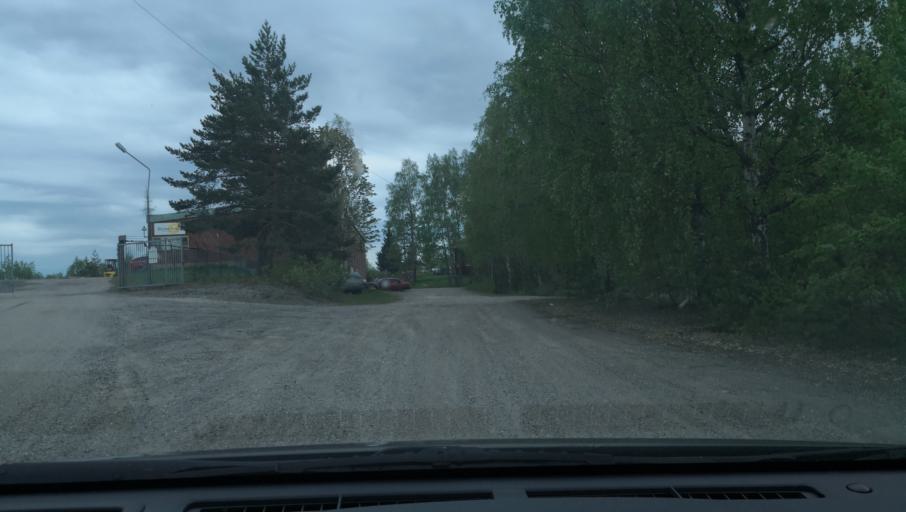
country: SE
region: Vaestmanland
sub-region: Skinnskattebergs Kommun
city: Skinnskatteberg
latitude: 59.8289
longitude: 15.5604
